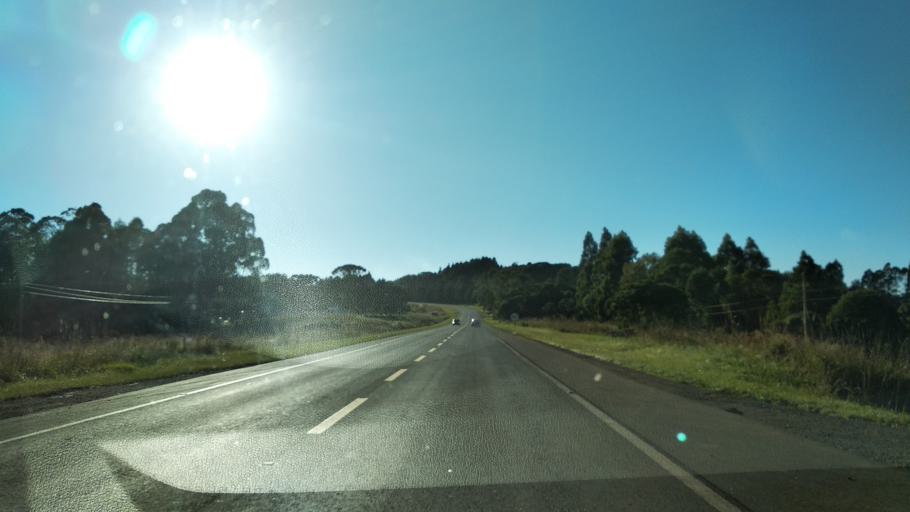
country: BR
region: Santa Catarina
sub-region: Lages
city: Lages
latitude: -27.7954
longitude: -50.3881
